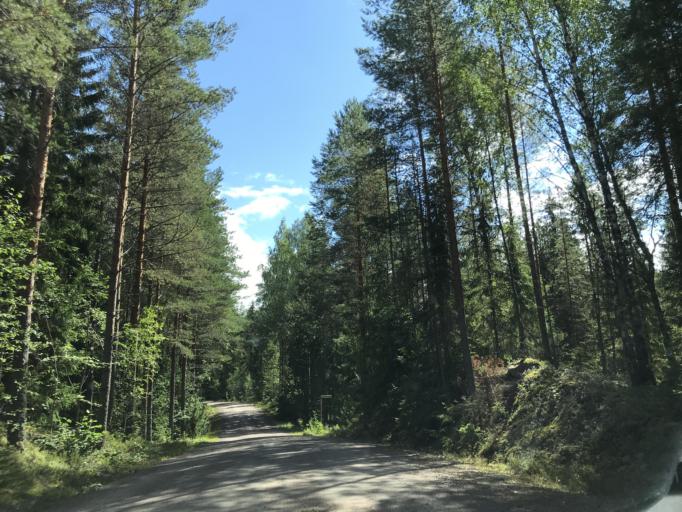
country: FI
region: Uusimaa
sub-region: Helsinki
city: Kaerkoelae
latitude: 60.6265
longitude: 23.7609
